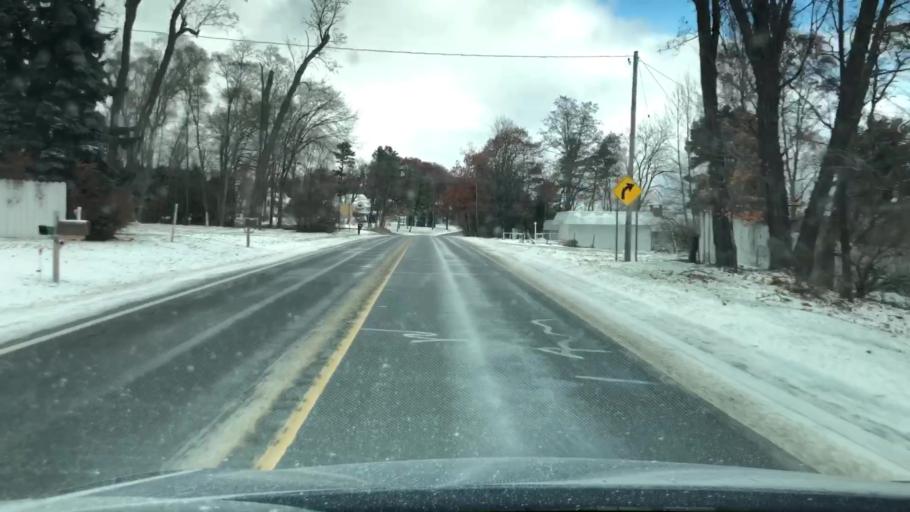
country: US
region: Michigan
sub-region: Grand Traverse County
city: Traverse City
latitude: 44.8206
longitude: -85.5542
